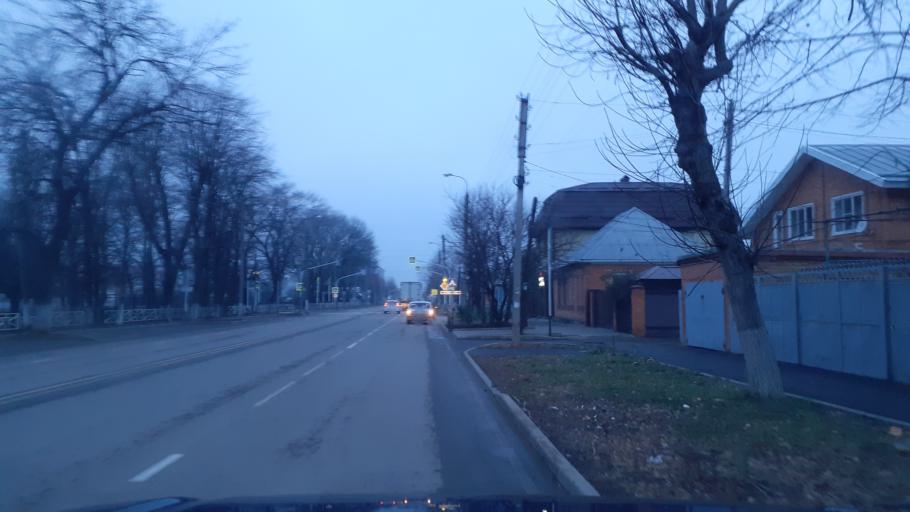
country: RU
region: Adygeya
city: Maykop
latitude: 44.6140
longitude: 40.0931
